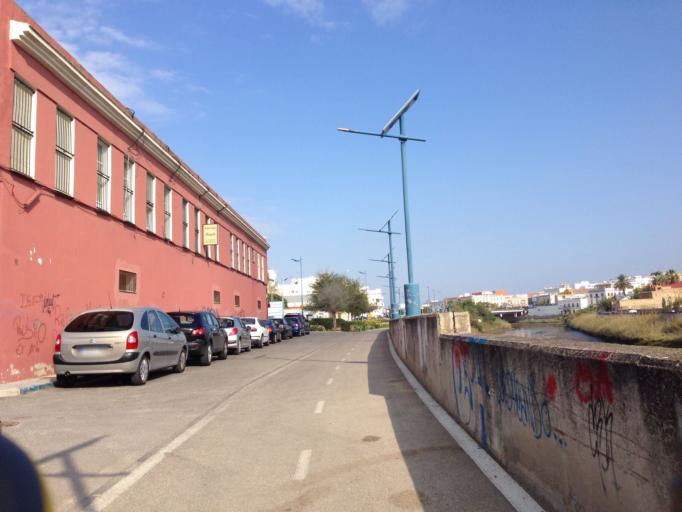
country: ES
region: Andalusia
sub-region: Provincia de Cadiz
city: Chiclana de la Frontera
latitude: 36.4171
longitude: -6.1431
